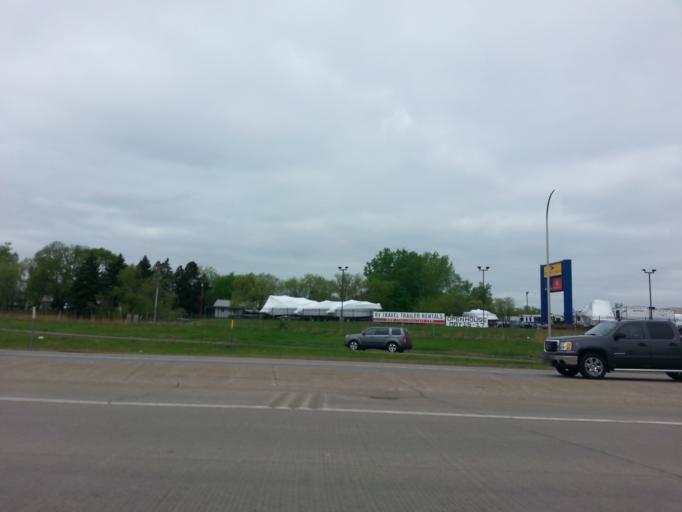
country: US
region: Minnesota
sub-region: Washington County
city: Oakdale
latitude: 44.9487
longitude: -92.9555
